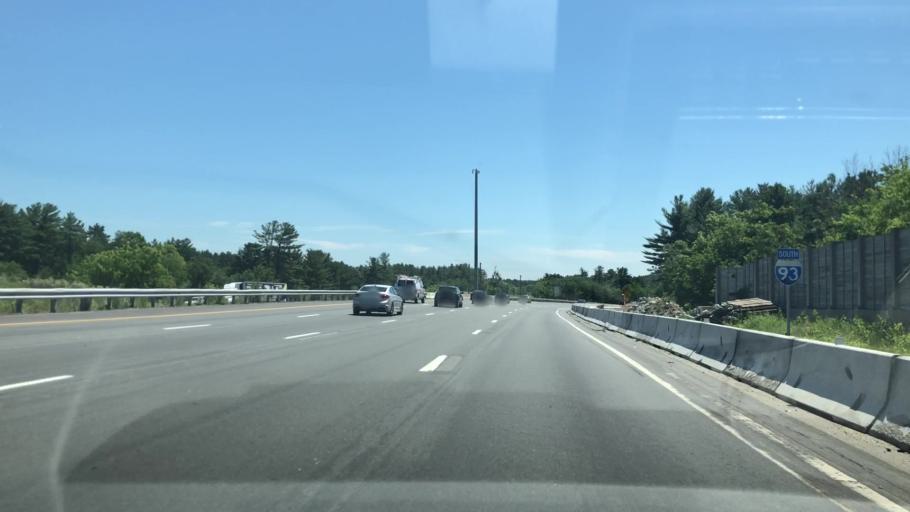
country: US
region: New Hampshire
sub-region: Hillsborough County
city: Manchester
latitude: 42.9552
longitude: -71.4049
